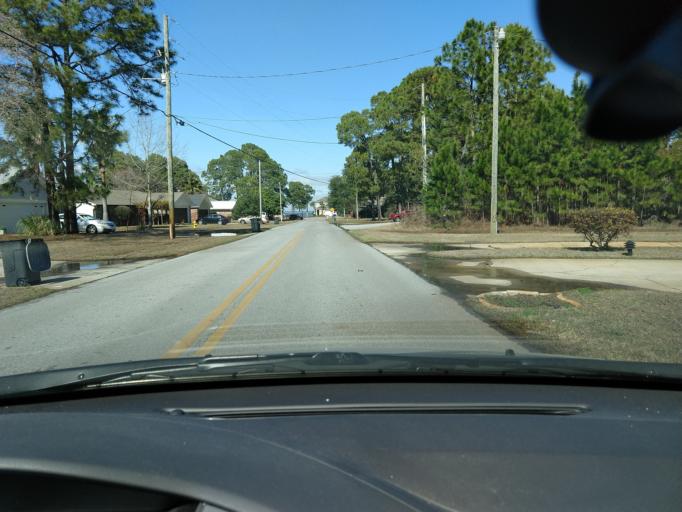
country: US
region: Florida
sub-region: Walton County
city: Miramar Beach
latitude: 30.3863
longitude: -86.3678
